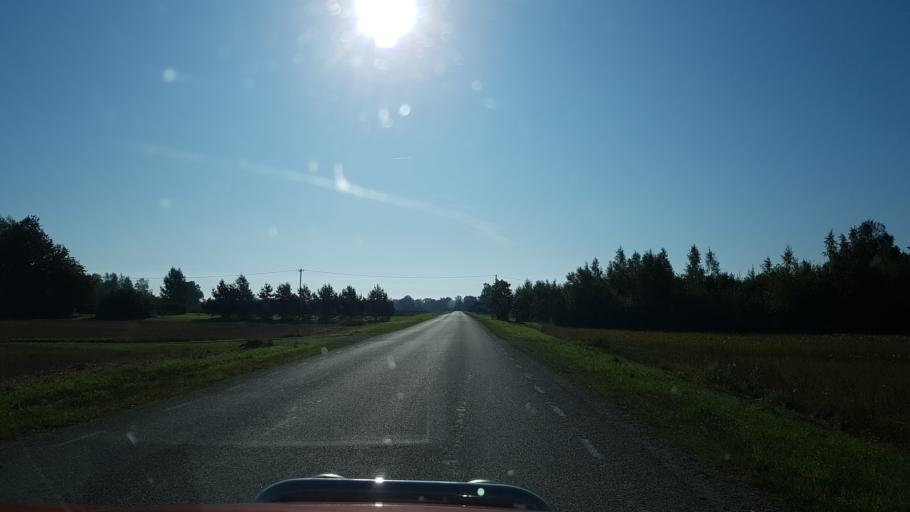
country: EE
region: Jogevamaa
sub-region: Tabivere vald
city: Tabivere
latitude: 58.6751
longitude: 26.6746
